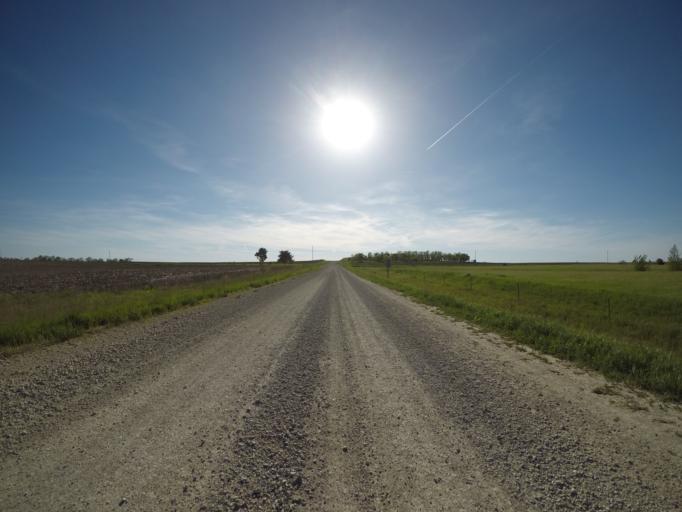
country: US
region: Kansas
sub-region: Clay County
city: Clay Center
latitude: 39.5100
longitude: -97.0698
